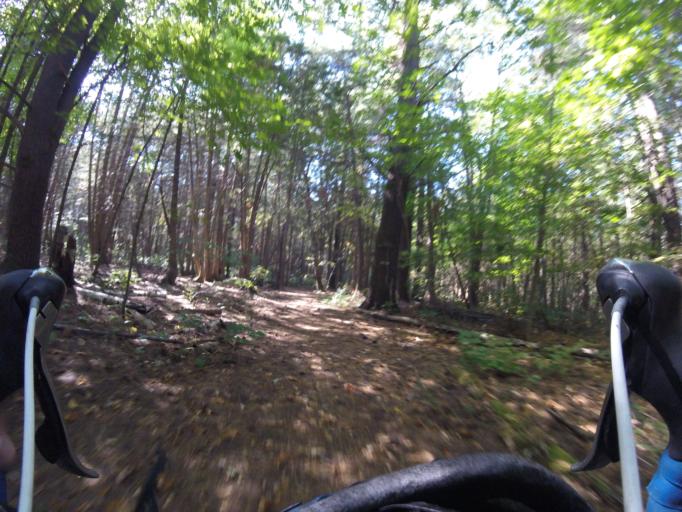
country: CA
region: Ontario
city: Bells Corners
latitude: 45.3040
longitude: -75.8898
